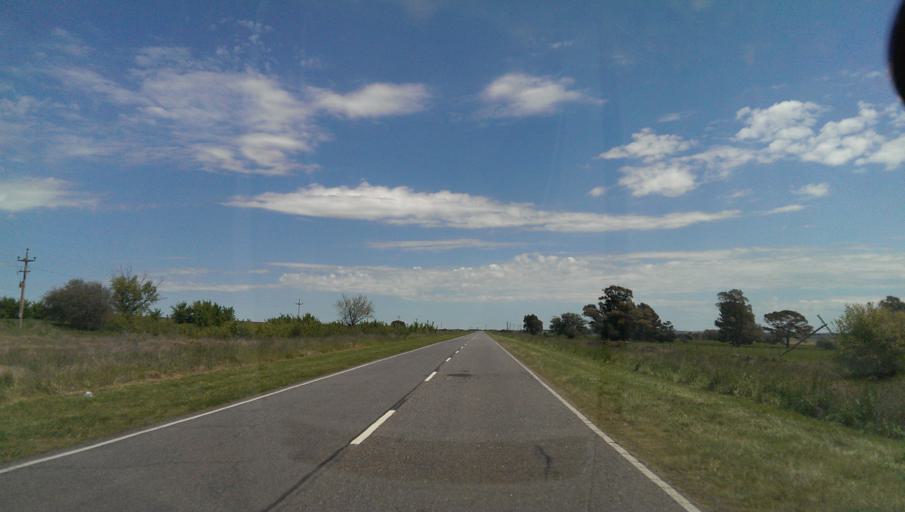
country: AR
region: Buenos Aires
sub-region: Partido de Tornquist
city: Tornquist
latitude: -38.0572
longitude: -62.1875
